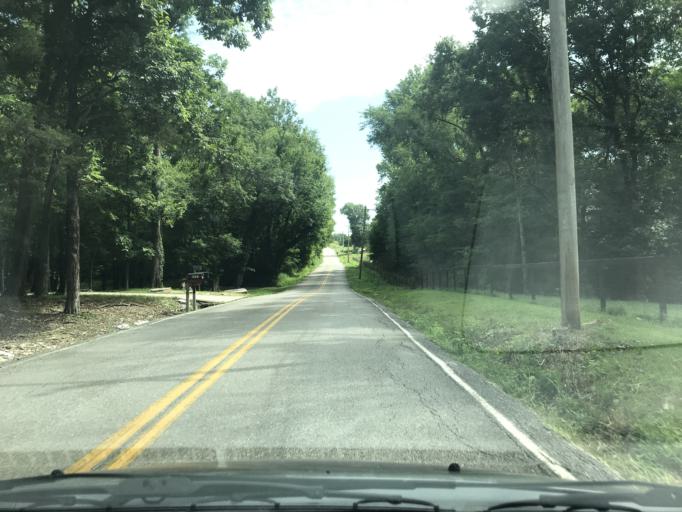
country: US
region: Tennessee
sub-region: Hamilton County
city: Lakesite
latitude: 35.1937
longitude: -85.0328
